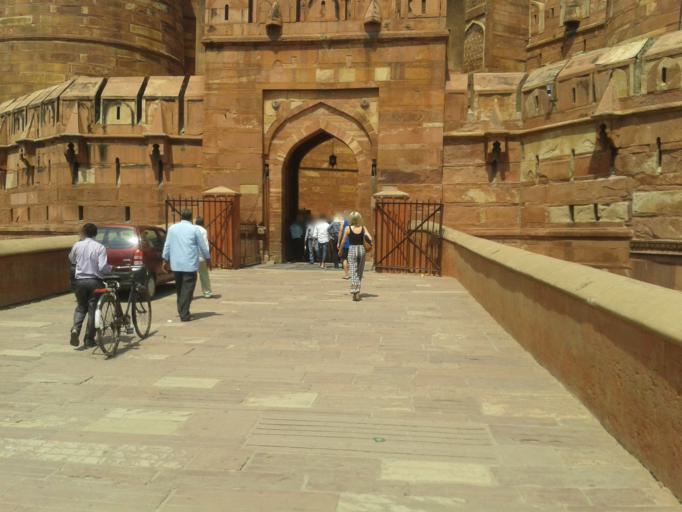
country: IN
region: Uttar Pradesh
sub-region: Agra
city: Agra
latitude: 27.1763
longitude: 78.0219
